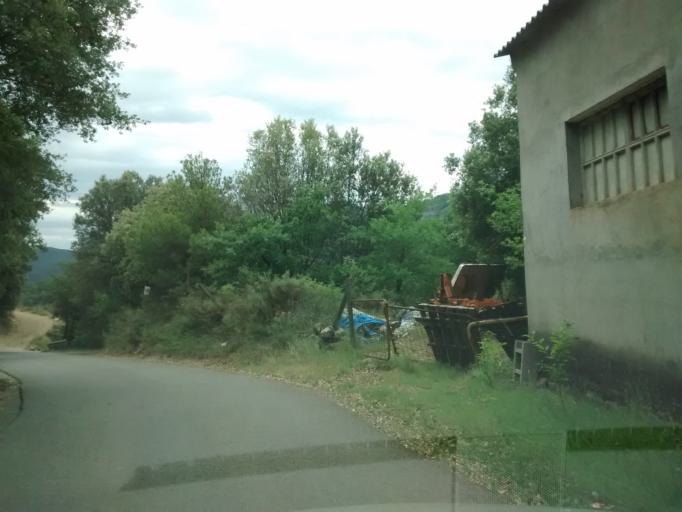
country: ES
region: Aragon
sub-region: Provincia de Huesca
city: Laspuna
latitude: 42.5044
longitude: 0.1390
